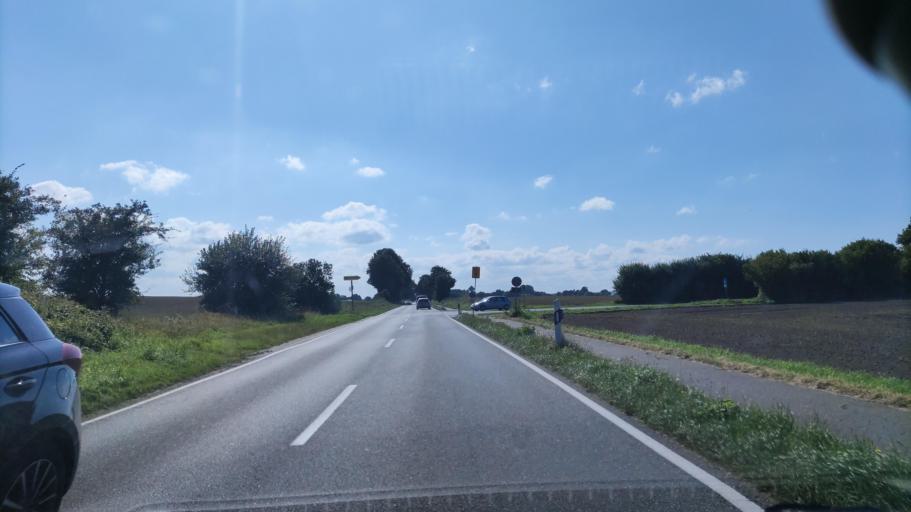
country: DE
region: Schleswig-Holstein
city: Osterby
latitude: 54.4572
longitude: 9.7687
